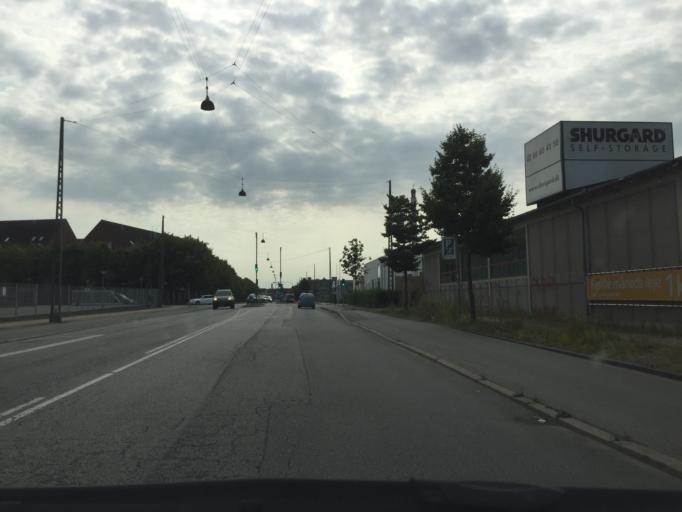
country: DK
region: Capital Region
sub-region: Frederiksberg Kommune
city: Frederiksberg
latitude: 55.7090
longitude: 12.5507
